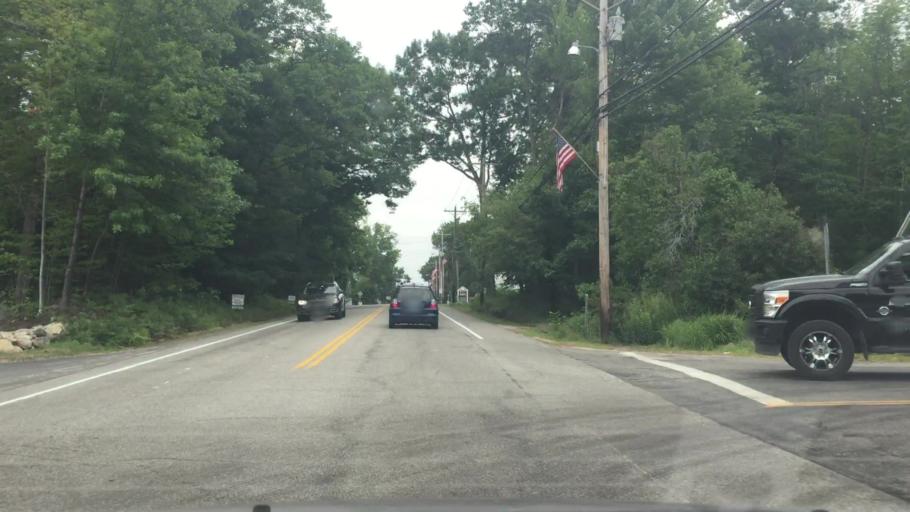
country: US
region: New Hampshire
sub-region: Carroll County
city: Moultonborough
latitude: 43.7506
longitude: -71.4010
